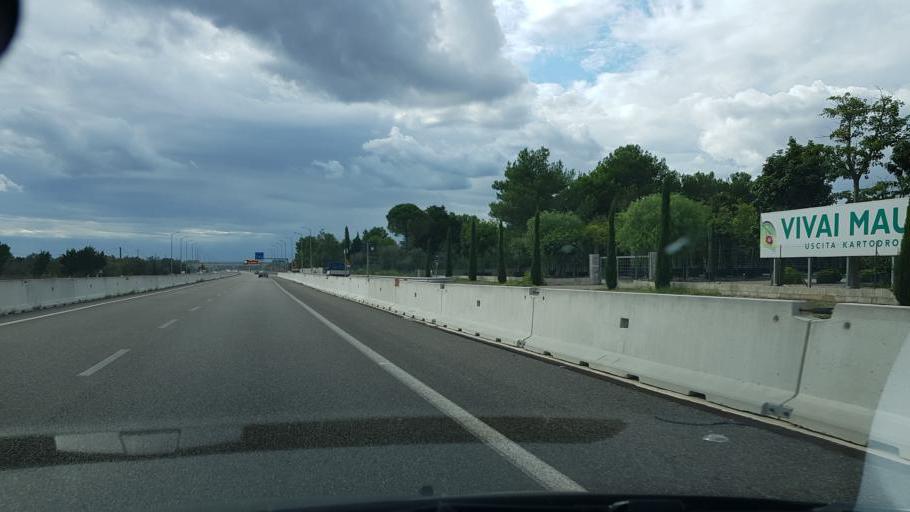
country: IT
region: Apulia
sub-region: Provincia di Lecce
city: Bagnolo del Salento
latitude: 40.1259
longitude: 18.3457
